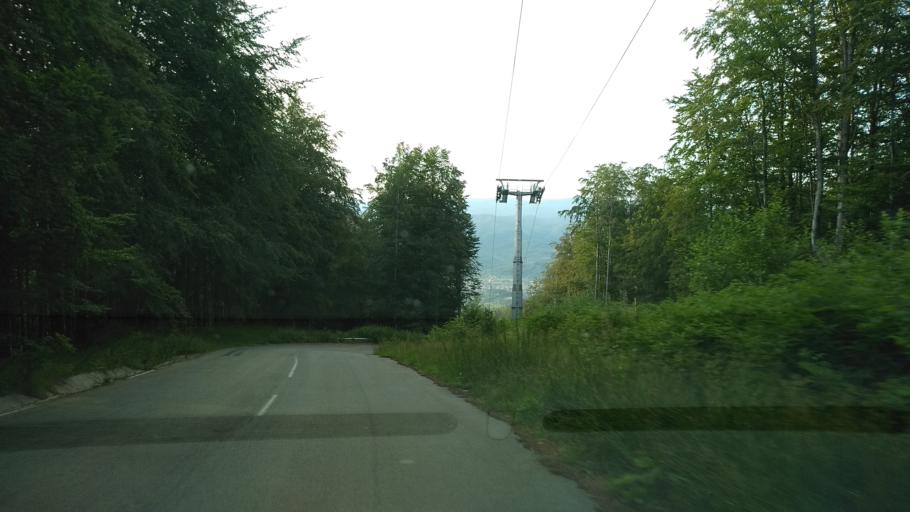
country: RO
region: Hunedoara
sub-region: Municipiul  Vulcan
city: Jiu-Paroseni
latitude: 45.3351
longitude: 23.2915
